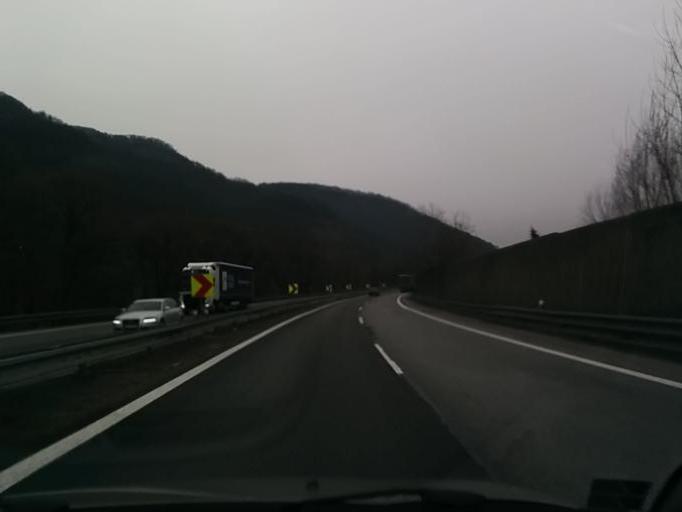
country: SK
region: Banskobystricky
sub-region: Okres Banska Bystrica
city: Banska Stiavnica
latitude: 48.5694
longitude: 18.9983
